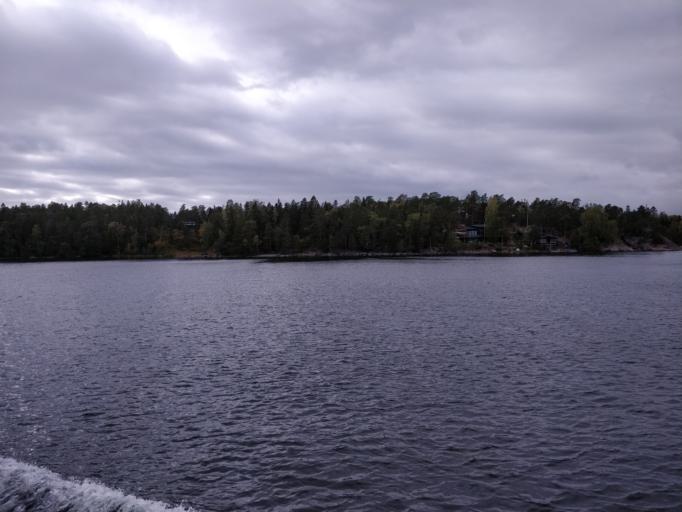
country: FI
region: Uusimaa
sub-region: Helsinki
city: Vantaa
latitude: 60.1690
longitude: 25.0968
